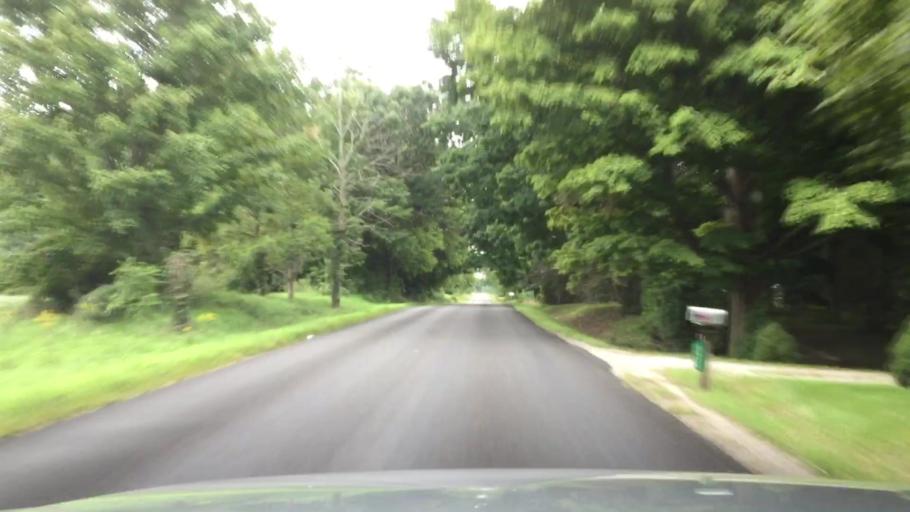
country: US
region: Michigan
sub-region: Shiawassee County
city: Durand
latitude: 42.8696
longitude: -84.0525
